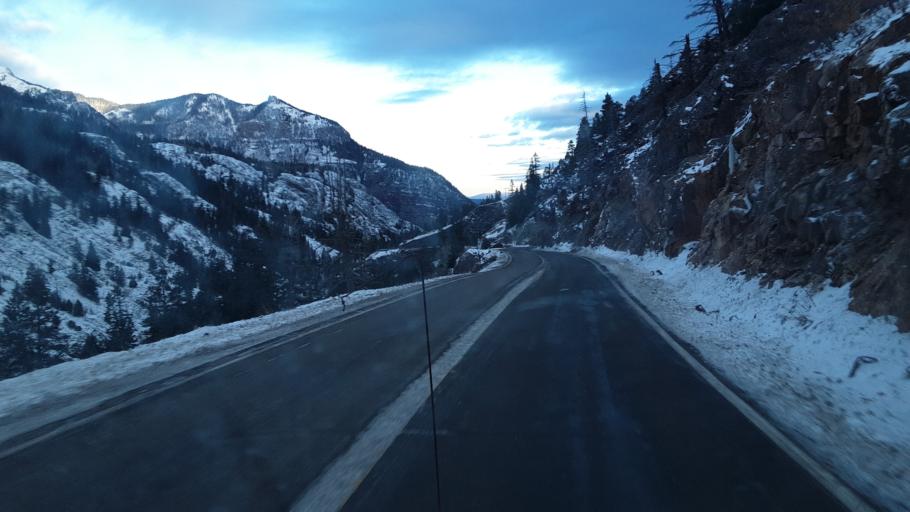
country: US
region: Colorado
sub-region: Ouray County
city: Ouray
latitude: 37.9945
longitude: -107.6568
